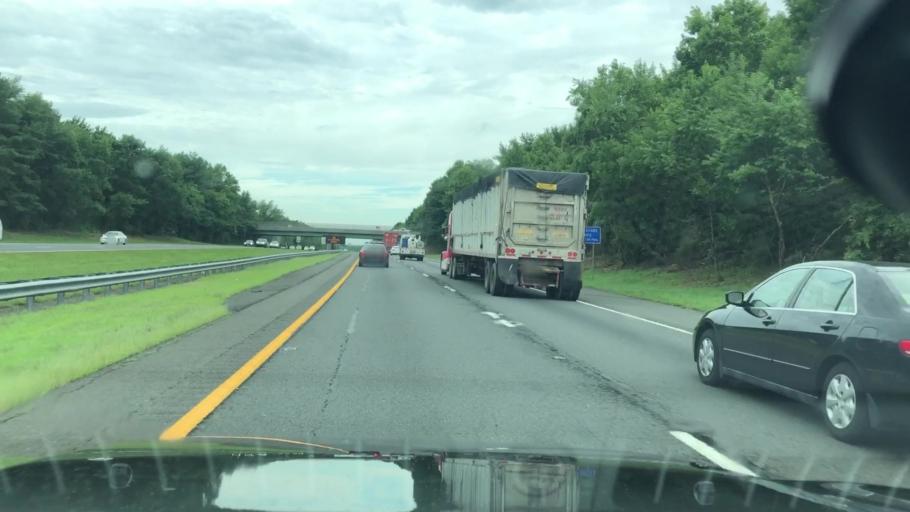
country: US
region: New Jersey
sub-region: Mercer County
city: Robbinsville
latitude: 40.1983
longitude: -74.6149
